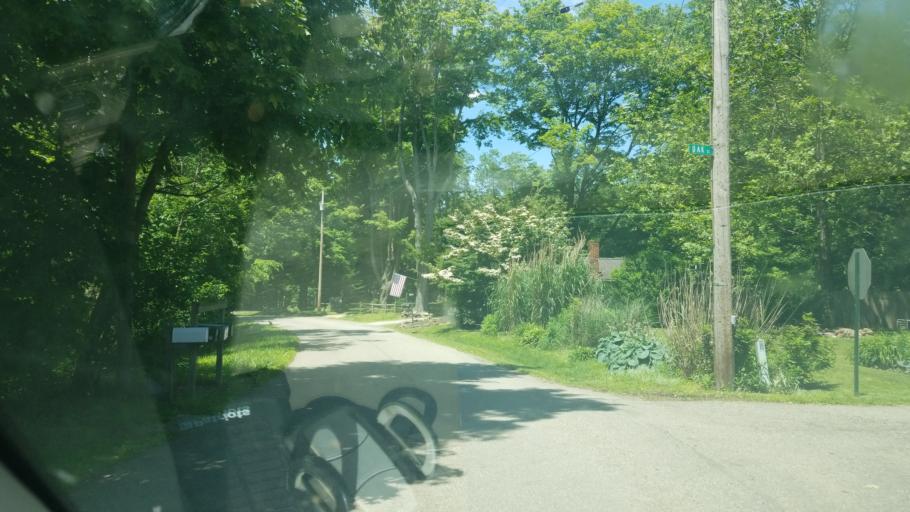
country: US
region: Ohio
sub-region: Mahoning County
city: Sebring
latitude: 40.8541
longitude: -80.9920
